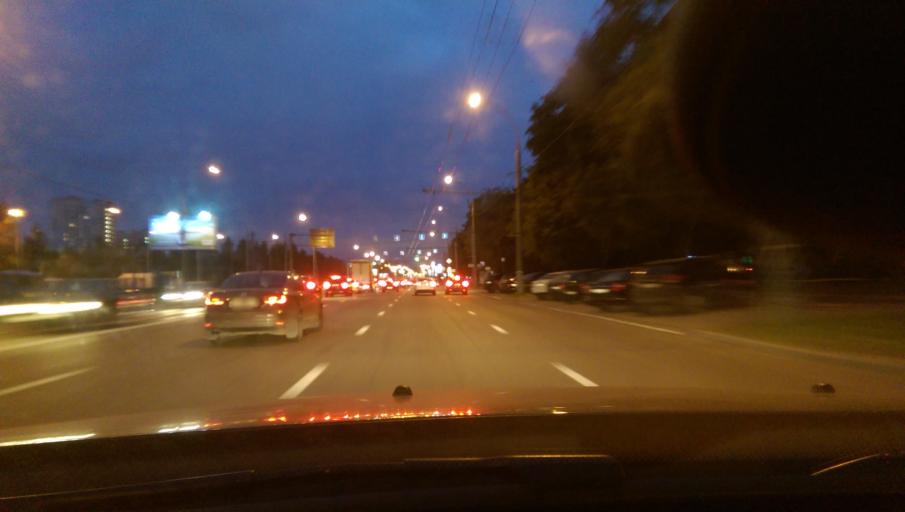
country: RU
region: Moscow
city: Vatutino
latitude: 55.8863
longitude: 37.6732
